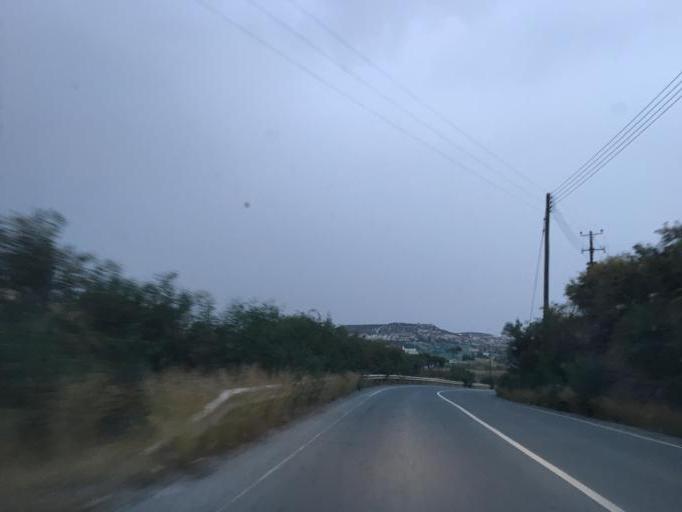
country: CY
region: Limassol
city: Parekklisha
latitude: 34.7601
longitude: 33.1598
